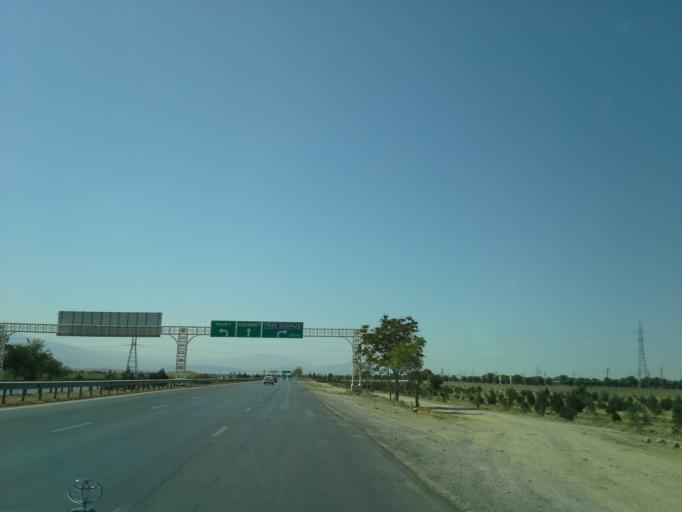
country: TM
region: Ahal
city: Annau
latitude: 37.9038
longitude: 58.5507
